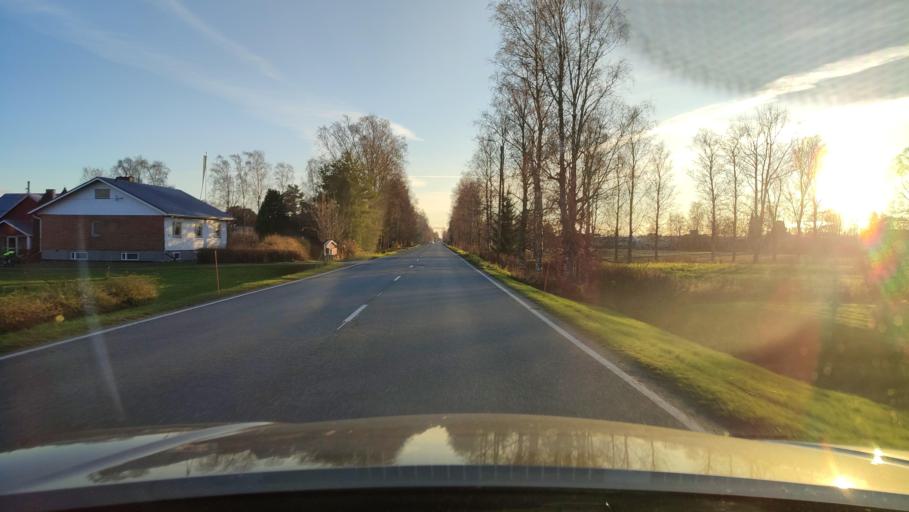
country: FI
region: Ostrobothnia
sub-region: Sydosterbotten
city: Naerpes
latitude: 62.5526
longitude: 21.4045
